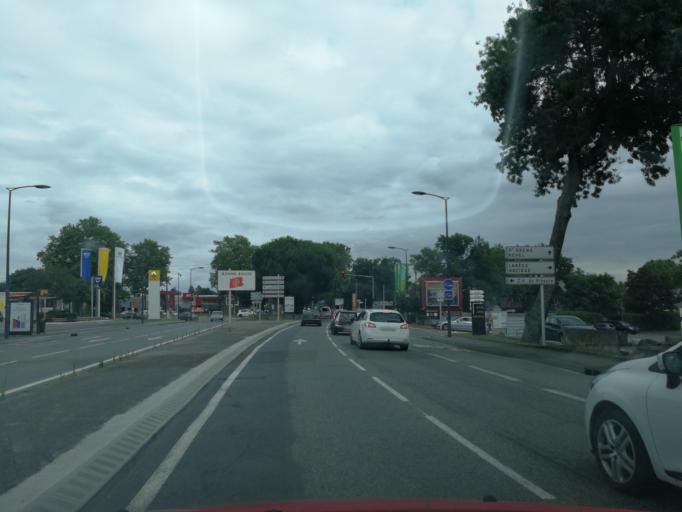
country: FR
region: Midi-Pyrenees
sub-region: Departement de la Haute-Garonne
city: Ramonville-Saint-Agne
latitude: 43.5718
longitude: 1.4973
